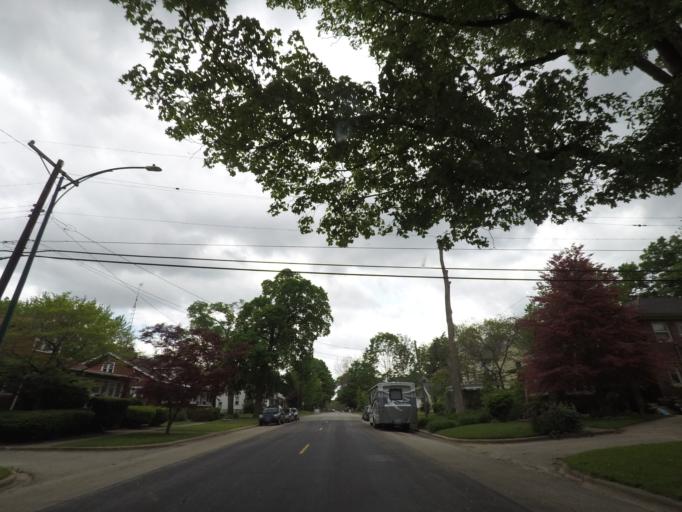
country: US
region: Illinois
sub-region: De Witt County
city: Clinton
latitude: 40.1506
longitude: -88.9604
